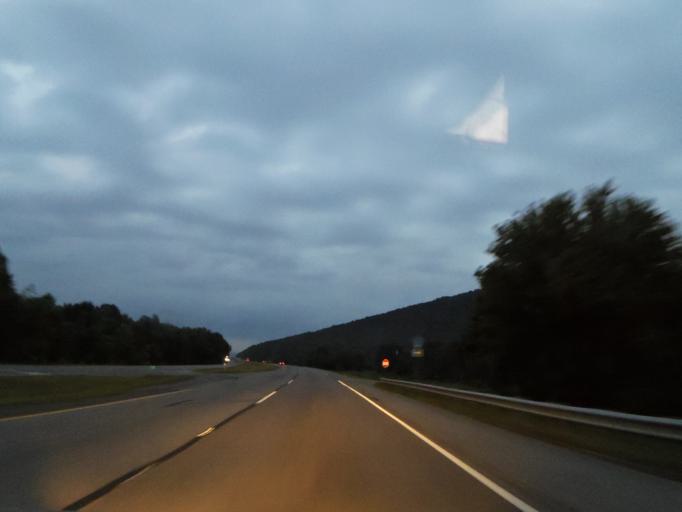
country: US
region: Alabama
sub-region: Madison County
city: New Hope
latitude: 34.6562
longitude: -86.3282
